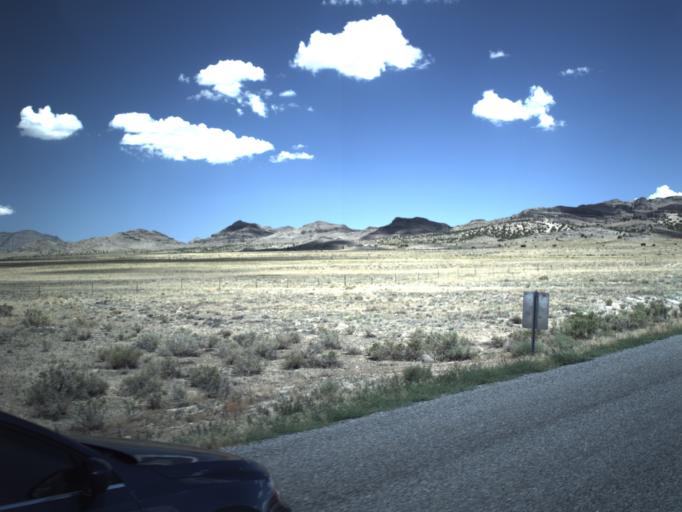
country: US
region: Utah
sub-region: Beaver County
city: Milford
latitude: 39.0667
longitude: -113.7384
